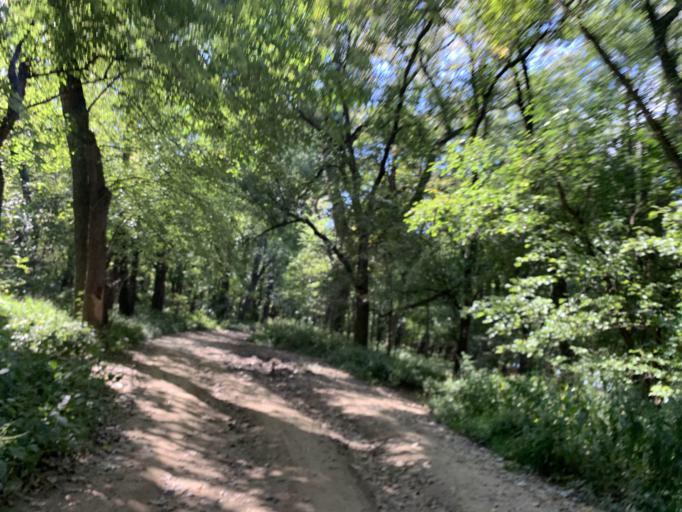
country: US
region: Indiana
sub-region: Floyd County
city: New Albany
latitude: 38.2796
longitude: -85.8052
